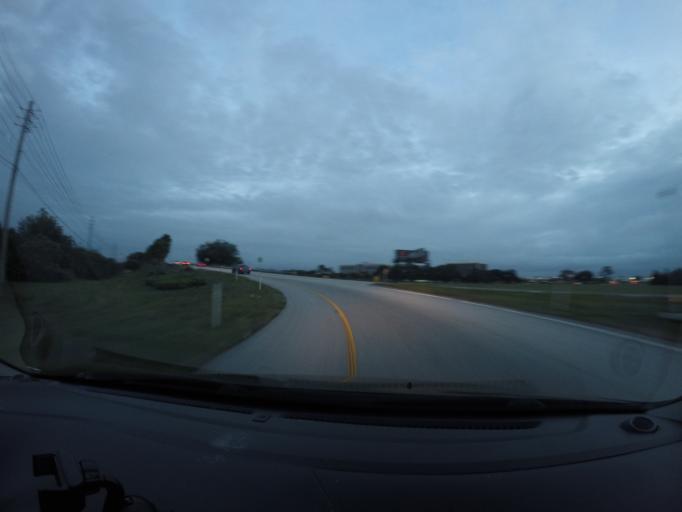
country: US
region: Florida
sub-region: Orange County
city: Tangelo Park
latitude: 28.4502
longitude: -81.4616
